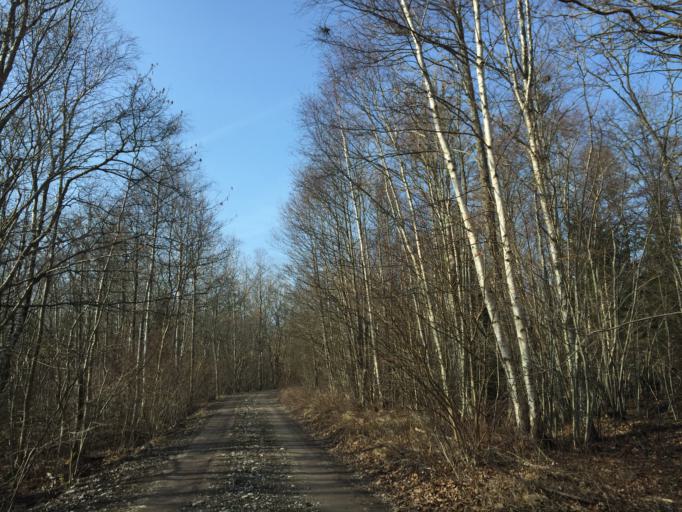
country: LV
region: Dundaga
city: Dundaga
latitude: 57.9311
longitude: 22.0246
